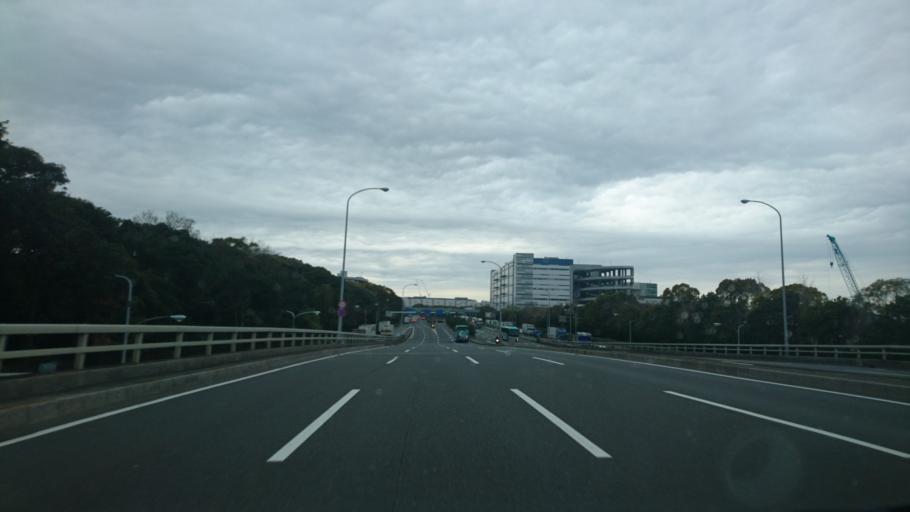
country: JP
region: Kanagawa
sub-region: Kawasaki-shi
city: Kawasaki
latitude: 35.5845
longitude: 139.7621
